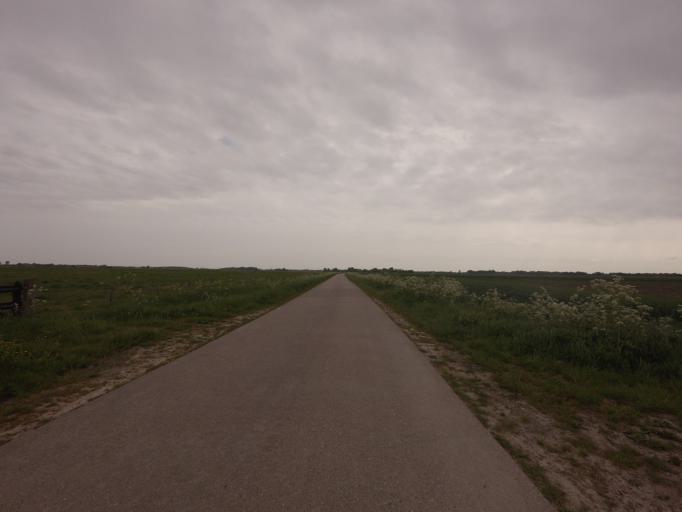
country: NL
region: Zeeland
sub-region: Gemeente Middelburg
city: Middelburg
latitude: 51.5231
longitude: 3.5775
